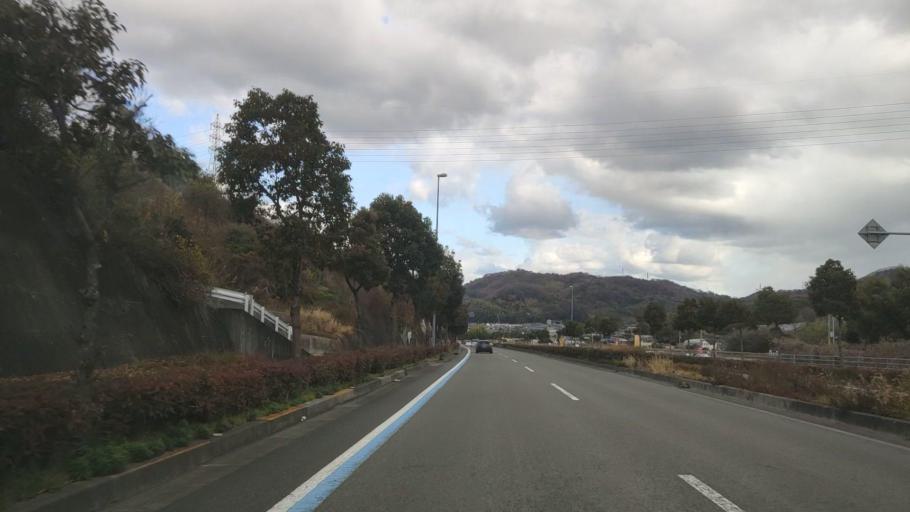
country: JP
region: Ehime
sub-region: Shikoku-chuo Shi
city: Matsuyama
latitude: 33.8922
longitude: 132.7575
